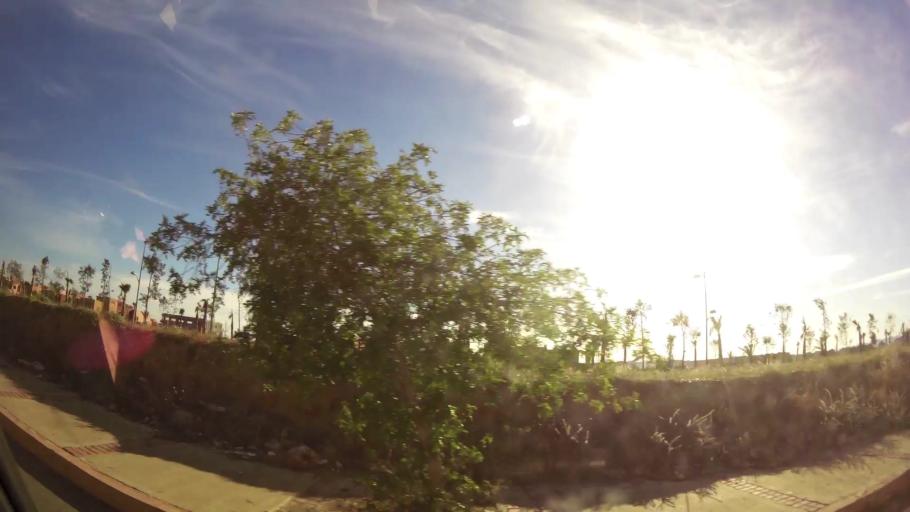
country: MA
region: Marrakech-Tensift-Al Haouz
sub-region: Marrakech
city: Marrakesh
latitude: 31.7518
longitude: -8.1089
